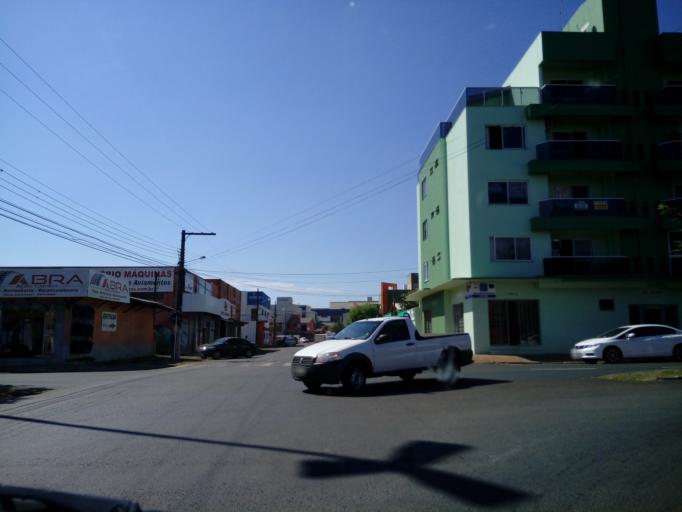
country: BR
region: Santa Catarina
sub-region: Chapeco
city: Chapeco
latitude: -27.0875
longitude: -52.6171
